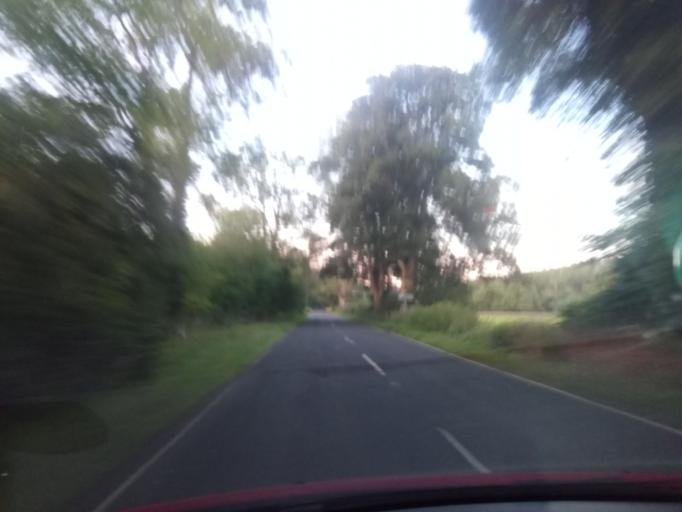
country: GB
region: England
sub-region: Northumberland
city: Bardon Mill
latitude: 54.9123
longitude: -2.3417
